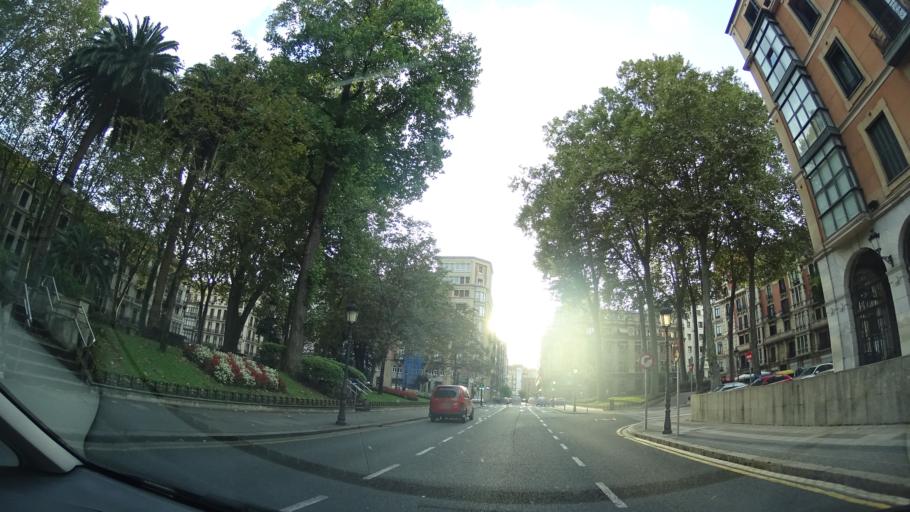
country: ES
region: Basque Country
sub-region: Bizkaia
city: Bilbao
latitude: 43.2631
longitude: -2.9281
